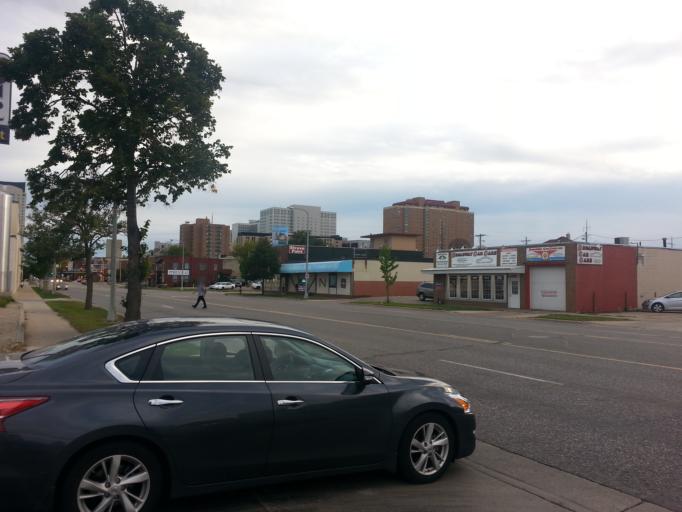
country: US
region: Minnesota
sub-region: Olmsted County
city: Rochester
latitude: 44.0289
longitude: -92.4629
